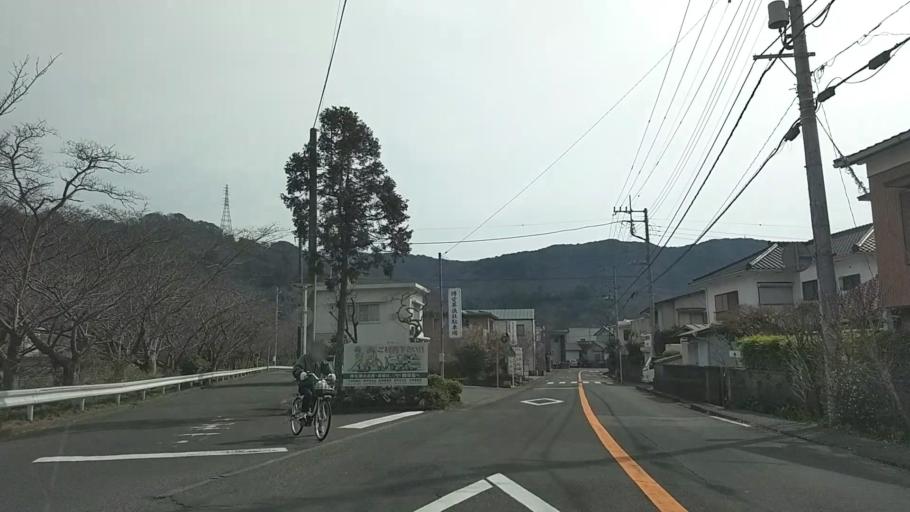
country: JP
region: Shizuoka
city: Shimoda
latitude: 34.6869
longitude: 138.9425
